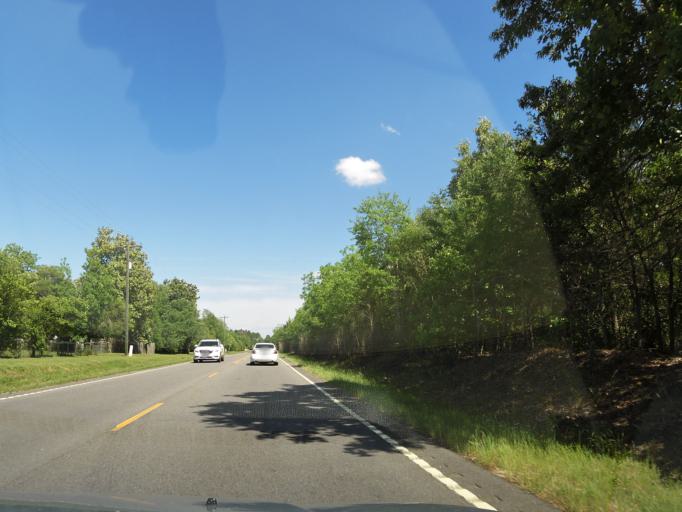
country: US
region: South Carolina
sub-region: Aiken County
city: Aiken
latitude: 33.5183
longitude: -81.5947
